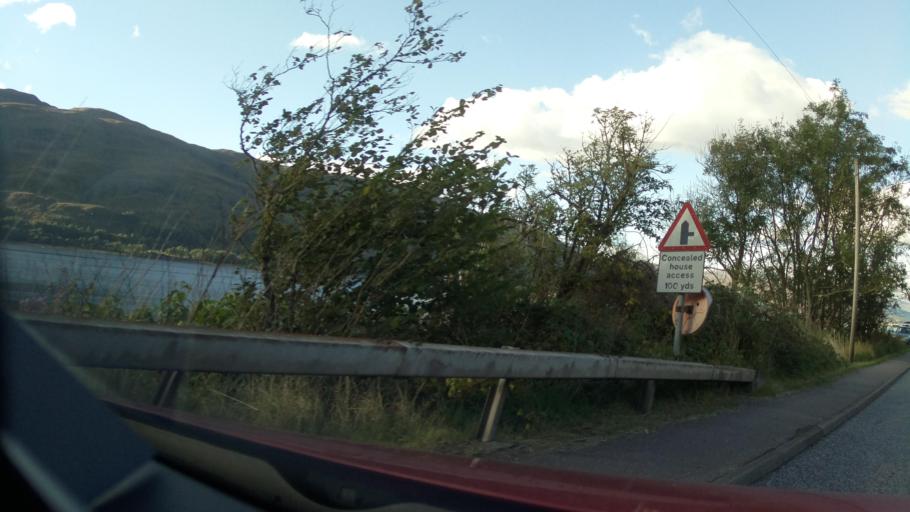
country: GB
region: Scotland
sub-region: Highland
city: Fort William
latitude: 56.8053
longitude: -5.1309
